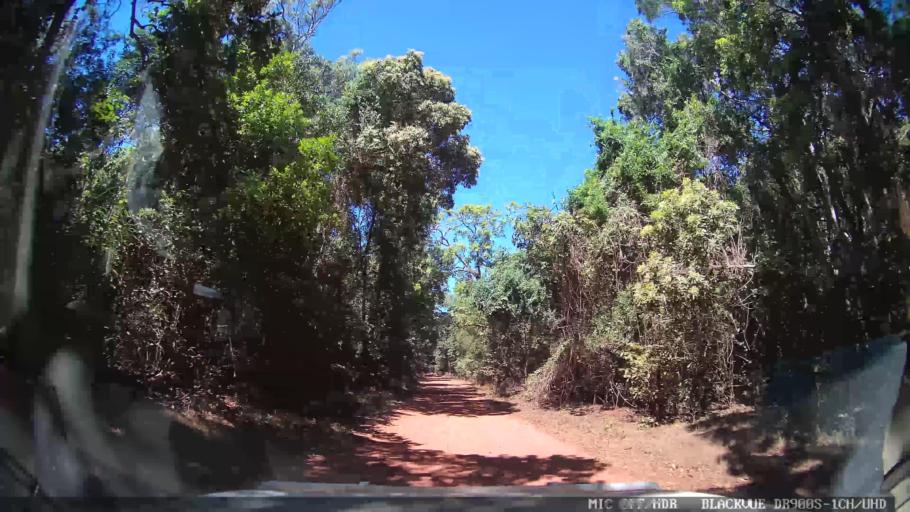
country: AU
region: Queensland
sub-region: Torres
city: Thursday Island
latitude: -10.7698
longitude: 142.5384
